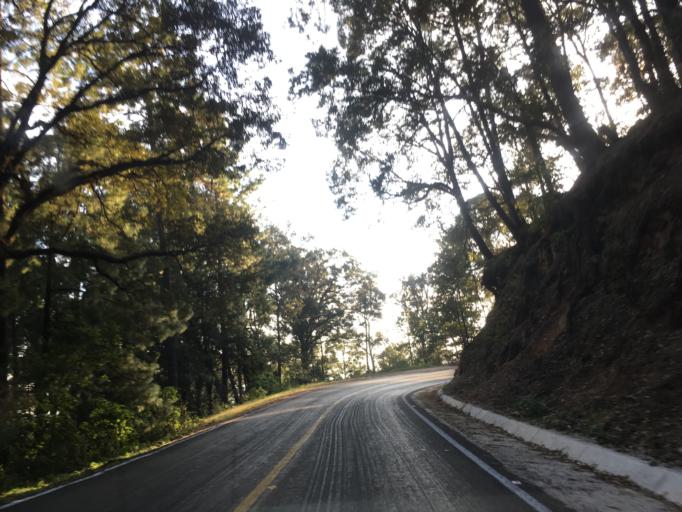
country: MX
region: Michoacan
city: Tzitzio
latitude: 19.6814
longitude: -100.8939
